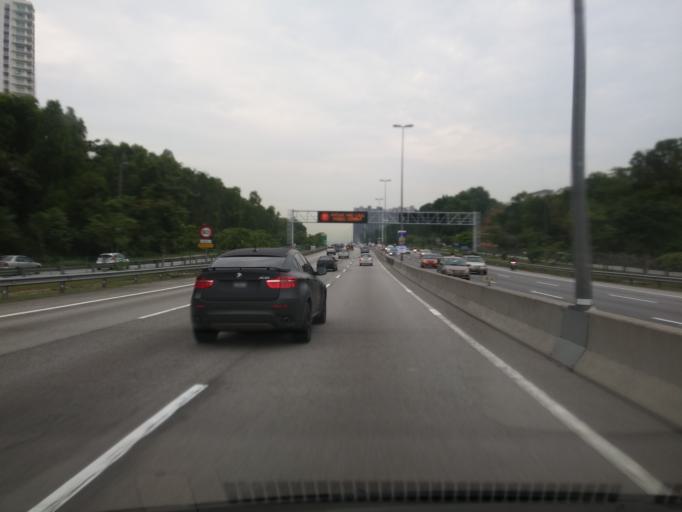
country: MY
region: Kuala Lumpur
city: Kuala Lumpur
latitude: 3.0764
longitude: 101.6901
